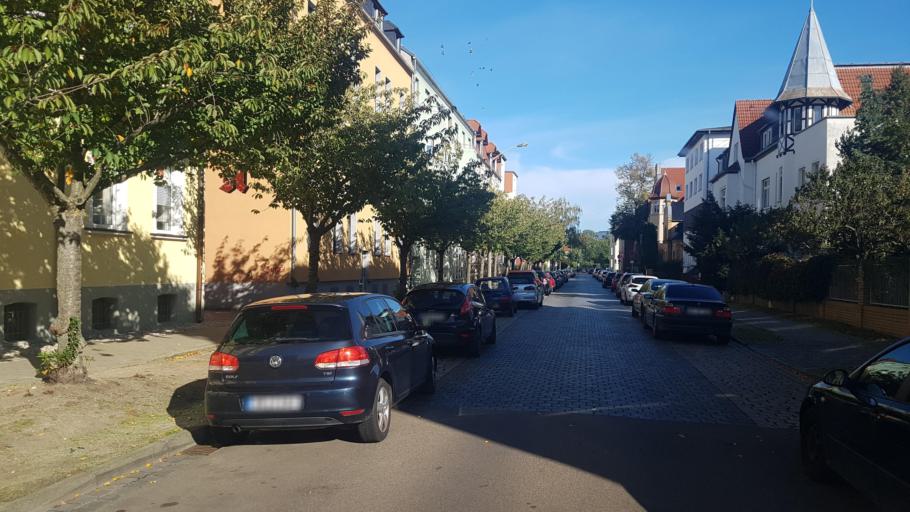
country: DE
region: Saxony-Anhalt
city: Wittenburg
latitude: 51.8692
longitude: 12.6538
